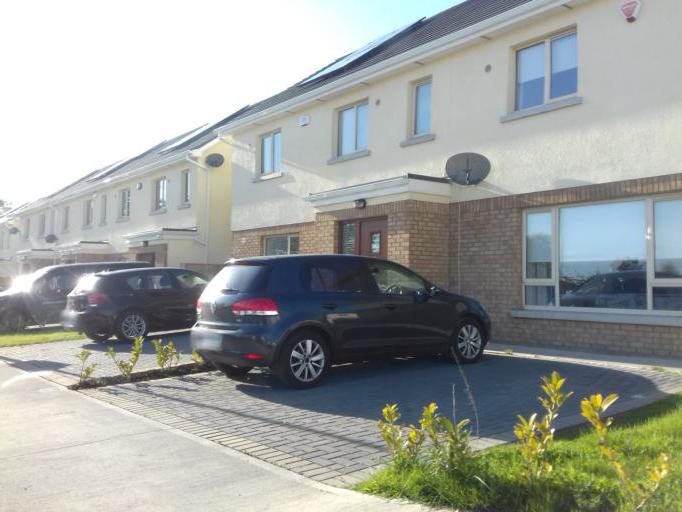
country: IE
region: Leinster
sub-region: Dublin City
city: Finglas
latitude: 53.3936
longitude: -6.3222
